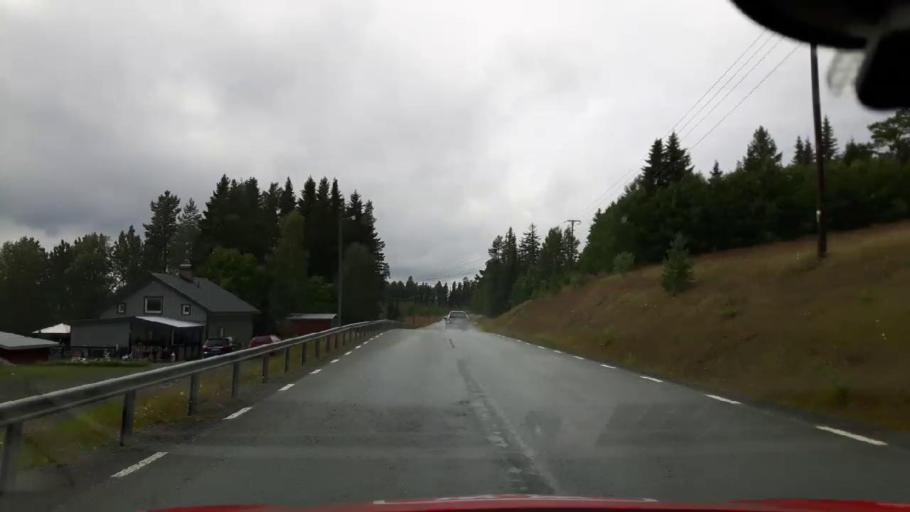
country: SE
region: Jaemtland
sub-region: Krokoms Kommun
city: Krokom
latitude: 63.3502
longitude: 14.1886
